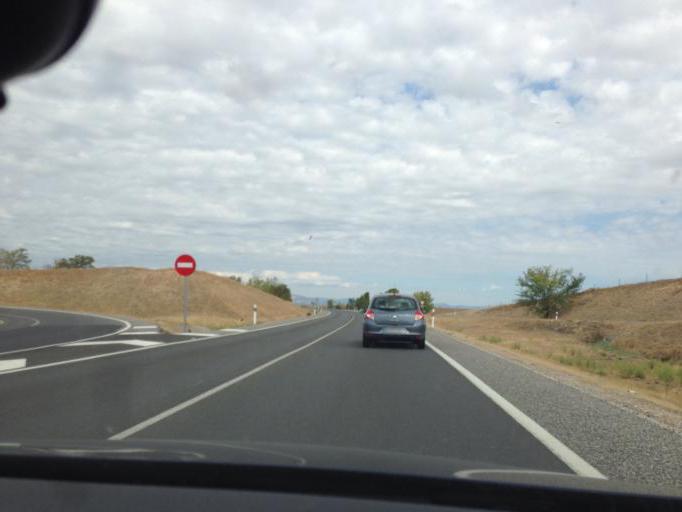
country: ES
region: Madrid
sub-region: Provincia de Madrid
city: Cobena
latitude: 40.5679
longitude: -3.5191
